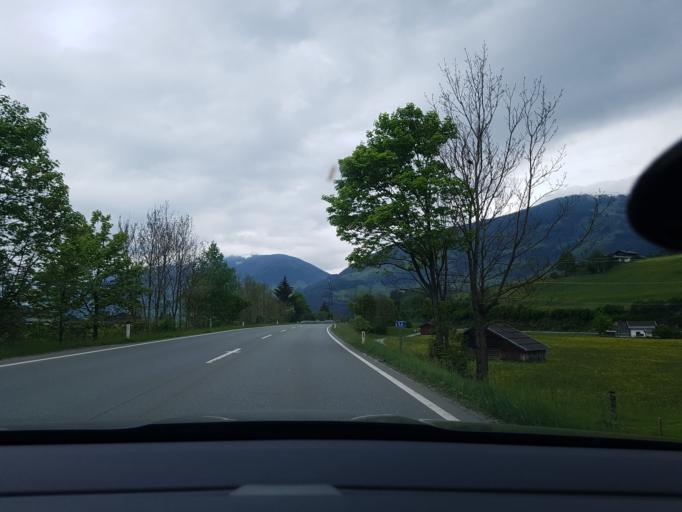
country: AT
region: Salzburg
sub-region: Politischer Bezirk Zell am See
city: Hollersbach im Pinzgau
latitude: 47.2763
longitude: 12.4256
